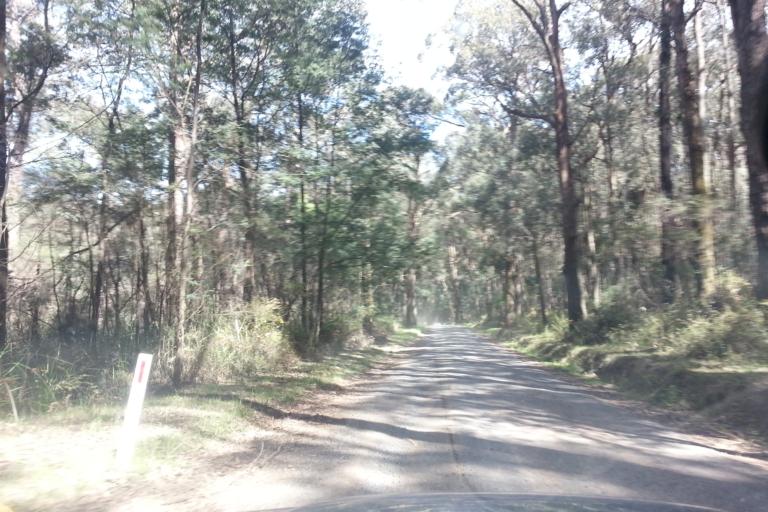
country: AU
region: Victoria
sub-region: Cardinia
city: Gembrook
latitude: -37.9328
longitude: 145.5674
